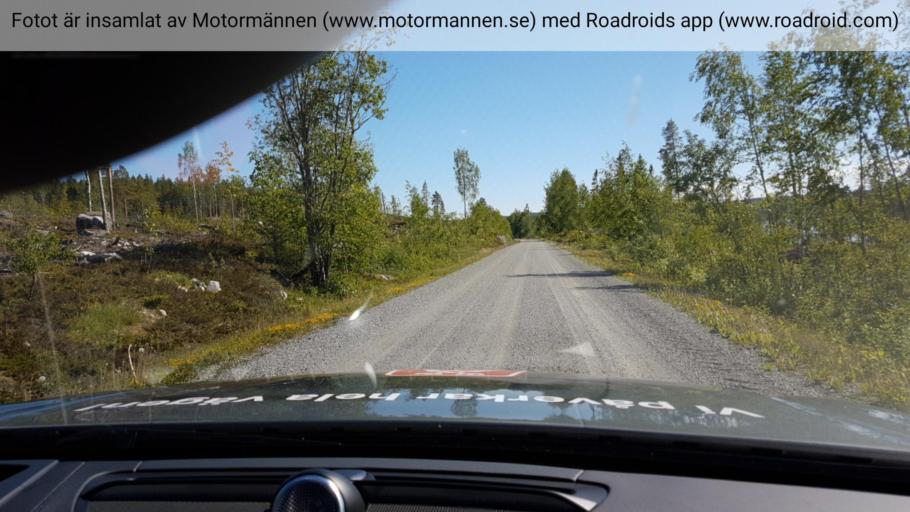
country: SE
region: Jaemtland
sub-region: Bergs Kommun
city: Hoverberg
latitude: 62.7461
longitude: 14.6630
